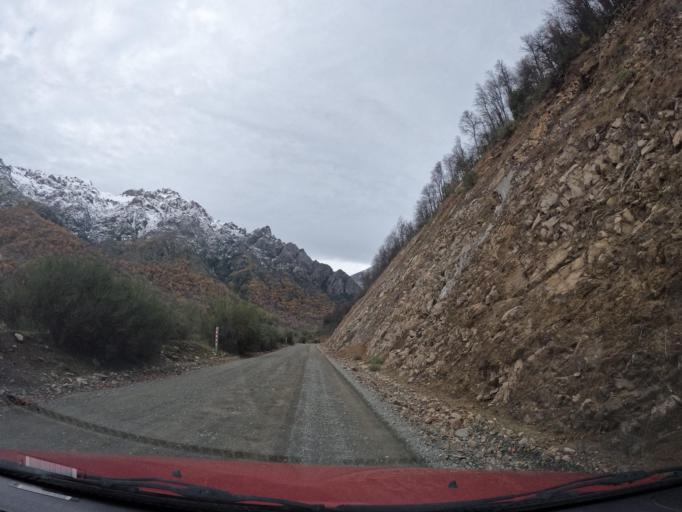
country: CL
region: Maule
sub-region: Provincia de Linares
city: Colbun
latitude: -35.8598
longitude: -71.1350
